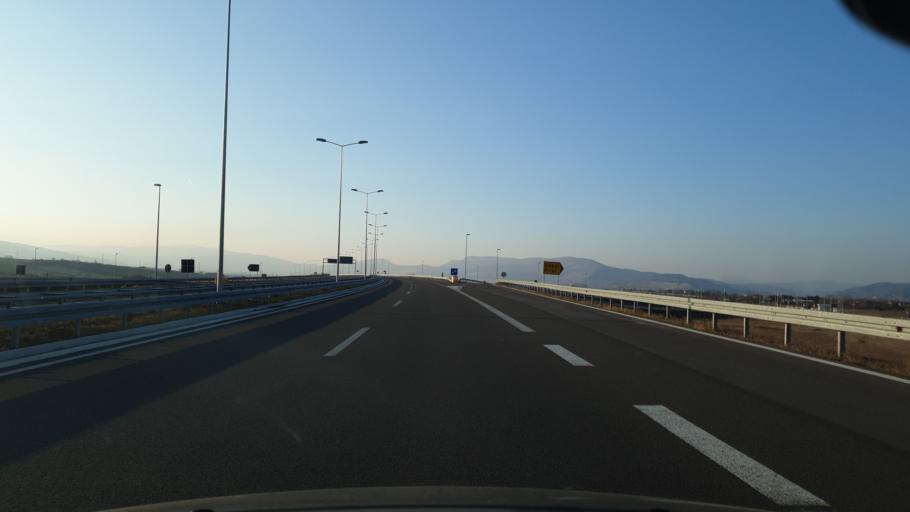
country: RS
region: Central Serbia
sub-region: Pirotski Okrug
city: Pirot
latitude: 43.1194
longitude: 22.6220
